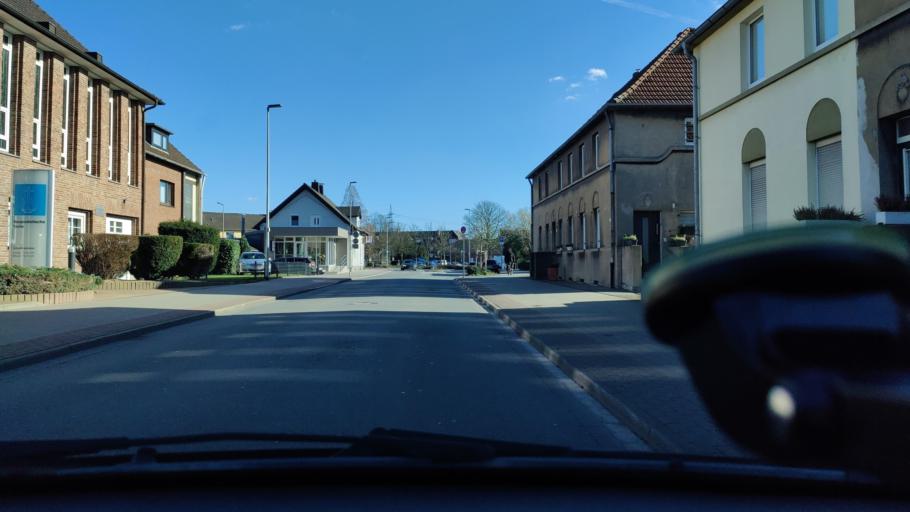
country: DE
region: North Rhine-Westphalia
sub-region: Regierungsbezirk Dusseldorf
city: Dinslaken
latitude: 51.5717
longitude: 6.7479
